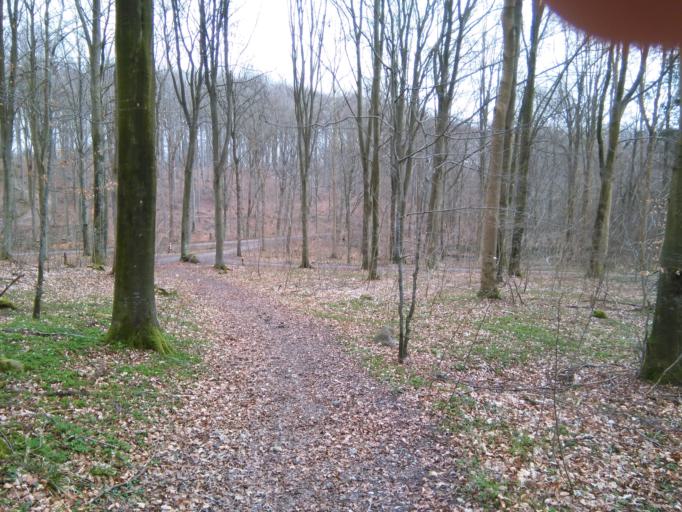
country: DK
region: Central Jutland
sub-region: Arhus Kommune
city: Beder
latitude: 56.0671
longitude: 10.2011
